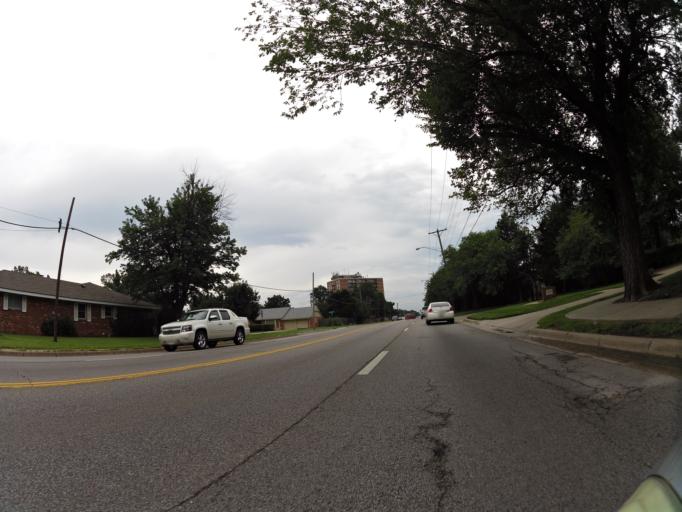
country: US
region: Kansas
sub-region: Sedgwick County
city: Bellaire
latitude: 37.7118
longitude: -97.2624
